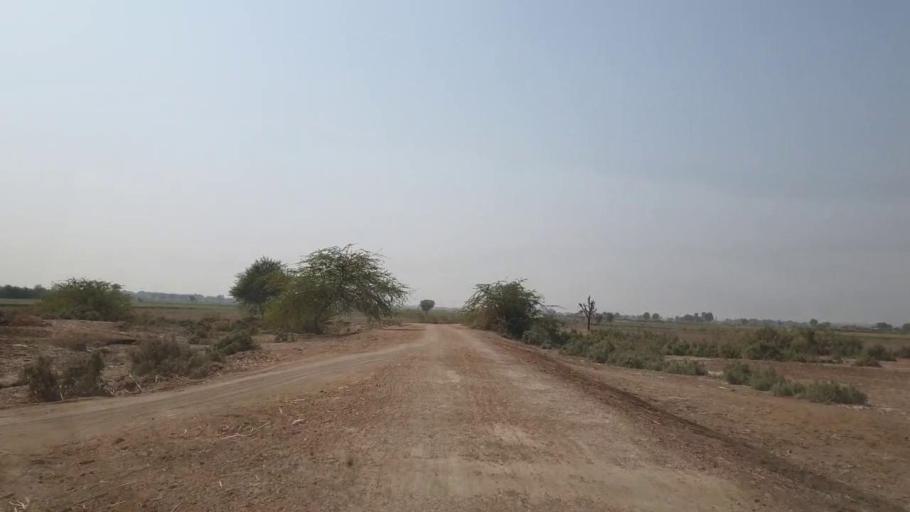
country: PK
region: Sindh
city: Mirpur Khas
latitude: 25.6571
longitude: 69.1313
